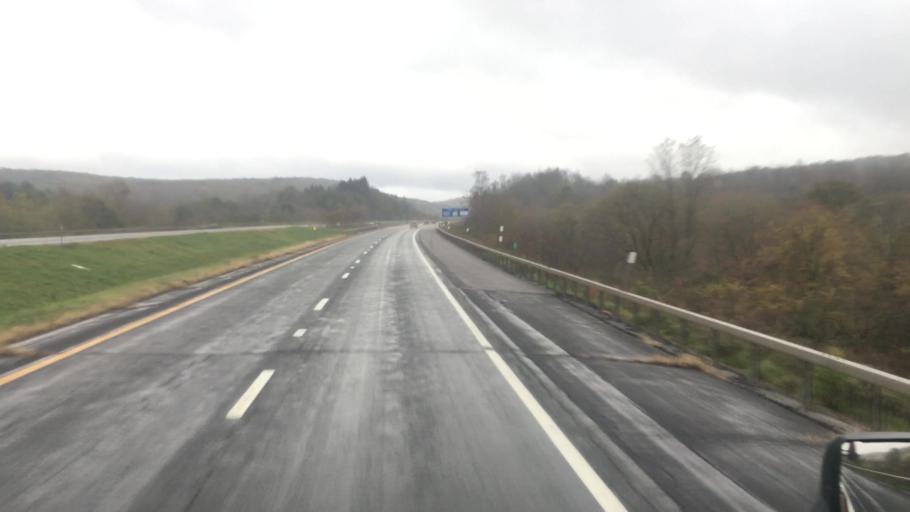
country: US
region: New York
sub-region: Chenango County
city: Bainbridge
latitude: 42.1843
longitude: -75.6173
